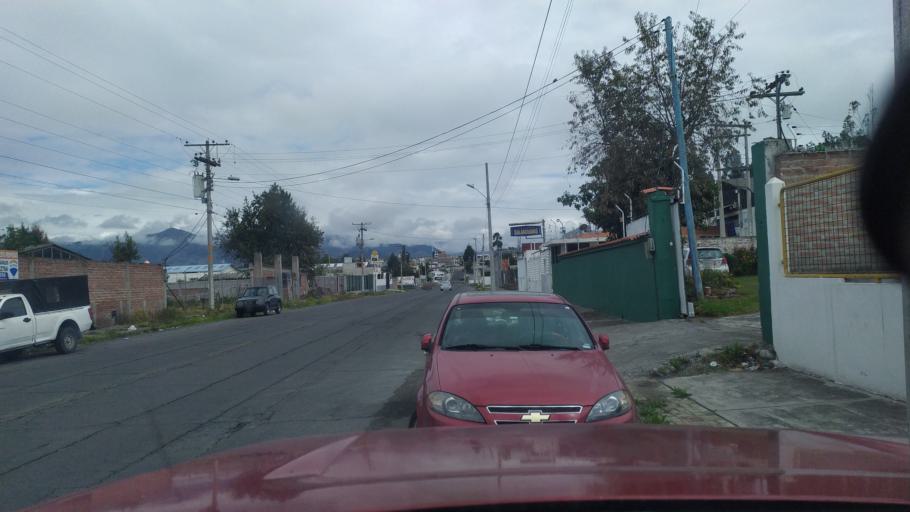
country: EC
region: Chimborazo
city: Riobamba
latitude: -1.6785
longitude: -78.6339
